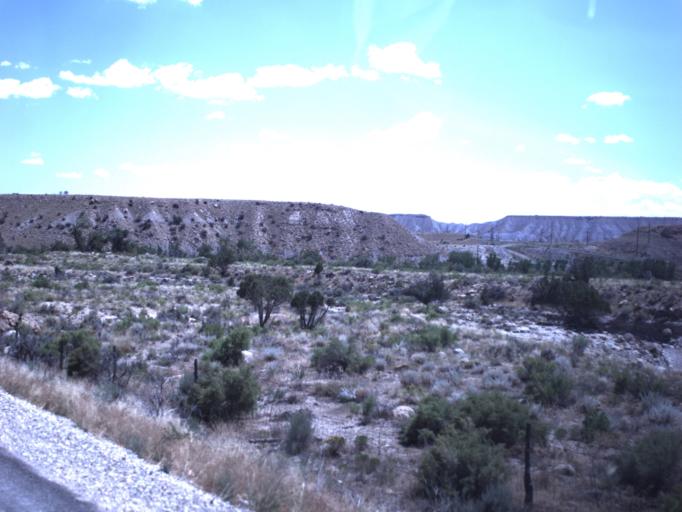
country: US
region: Utah
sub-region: Emery County
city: Orangeville
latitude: 39.2519
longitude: -111.0933
